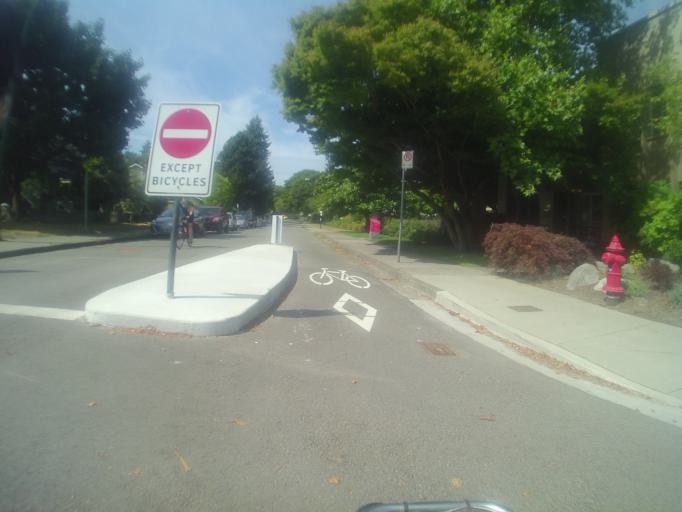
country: CA
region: British Columbia
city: West End
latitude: 49.2628
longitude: -123.1459
